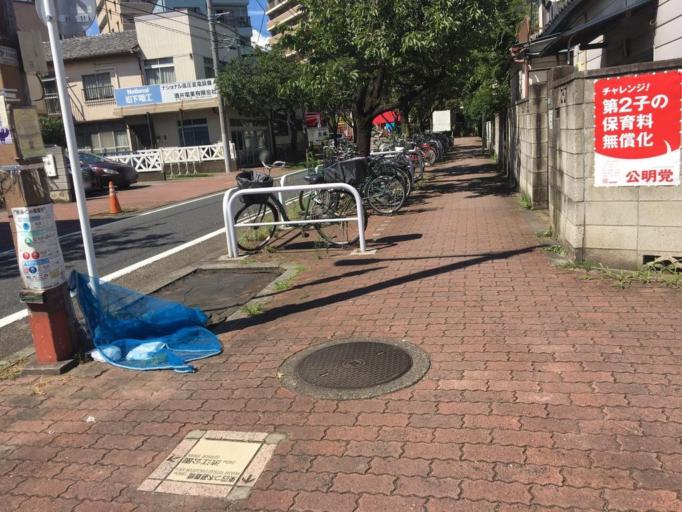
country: JP
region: Chiba
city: Matsudo
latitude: 35.7358
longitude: 139.8463
